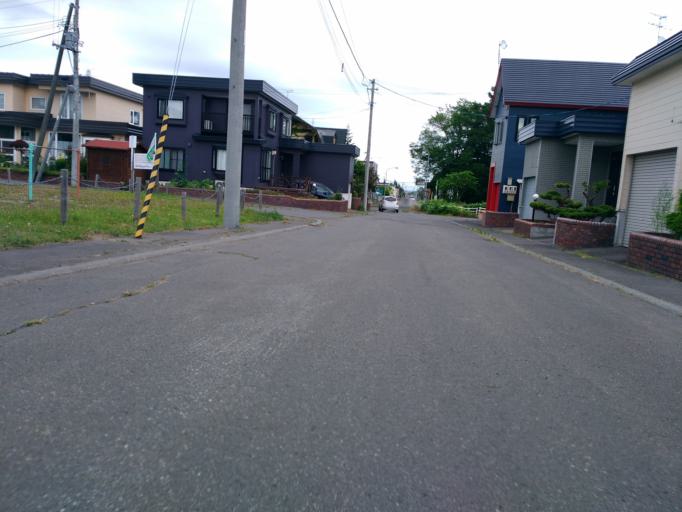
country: JP
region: Hokkaido
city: Ebetsu
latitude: 43.0785
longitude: 141.5219
